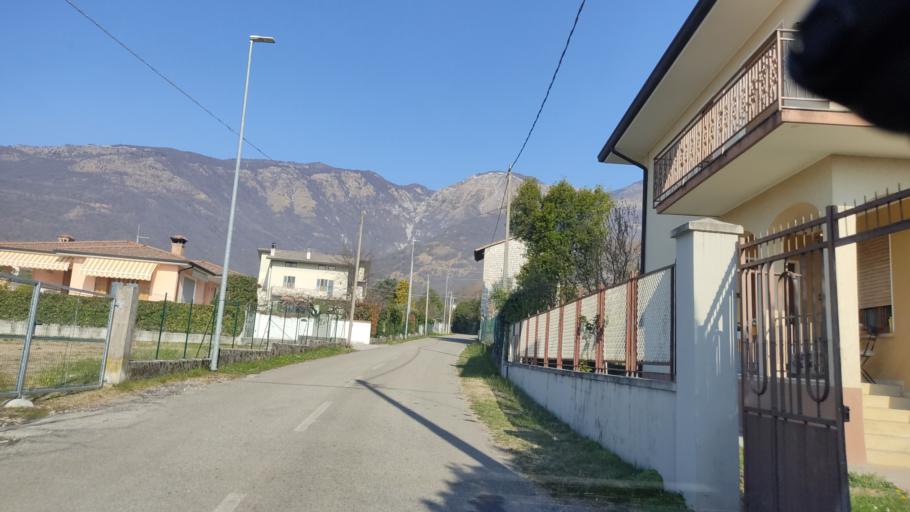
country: IT
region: Friuli Venezia Giulia
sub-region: Provincia di Pordenone
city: Budoia
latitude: 46.0550
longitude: 12.5401
